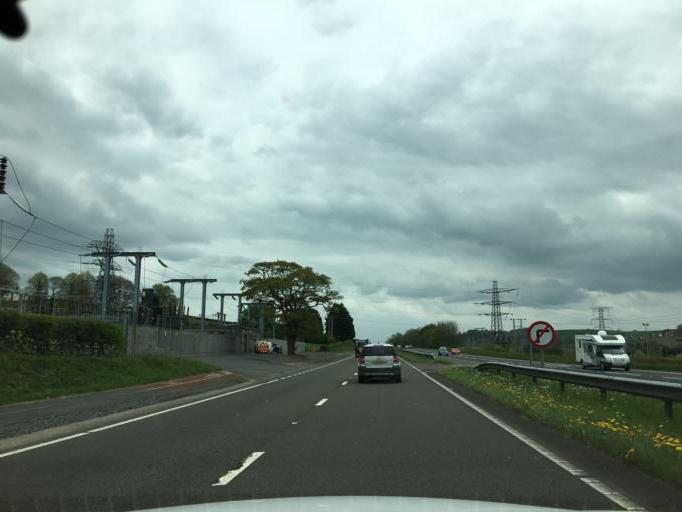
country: GB
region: Wales
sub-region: Carmarthenshire
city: Llangain
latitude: 51.8473
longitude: -4.3580
